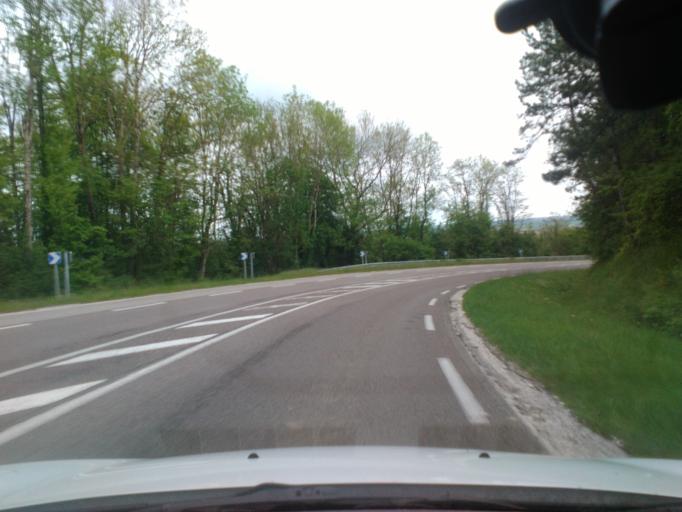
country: FR
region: Champagne-Ardenne
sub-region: Departement de la Haute-Marne
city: Chaumont
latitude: 48.1403
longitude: 5.0507
